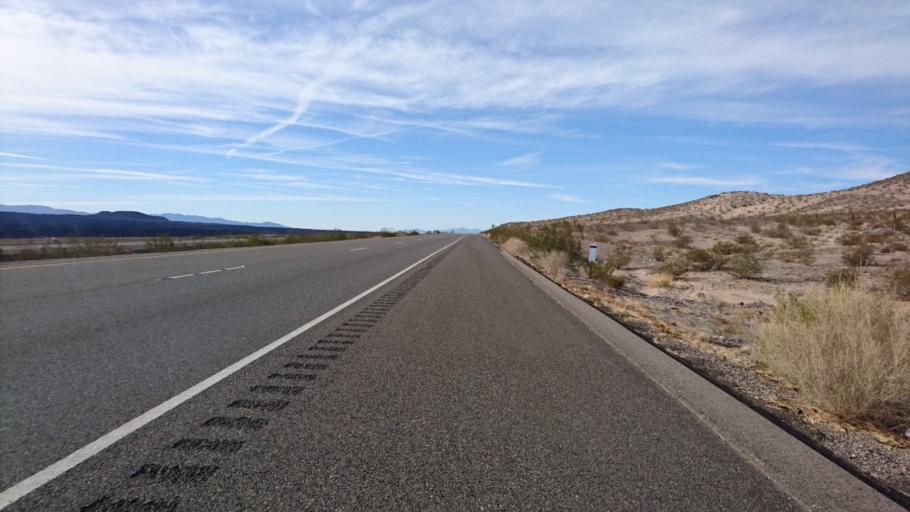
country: US
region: California
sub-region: San Bernardino County
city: Joshua Tree
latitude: 34.7464
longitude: -116.3267
